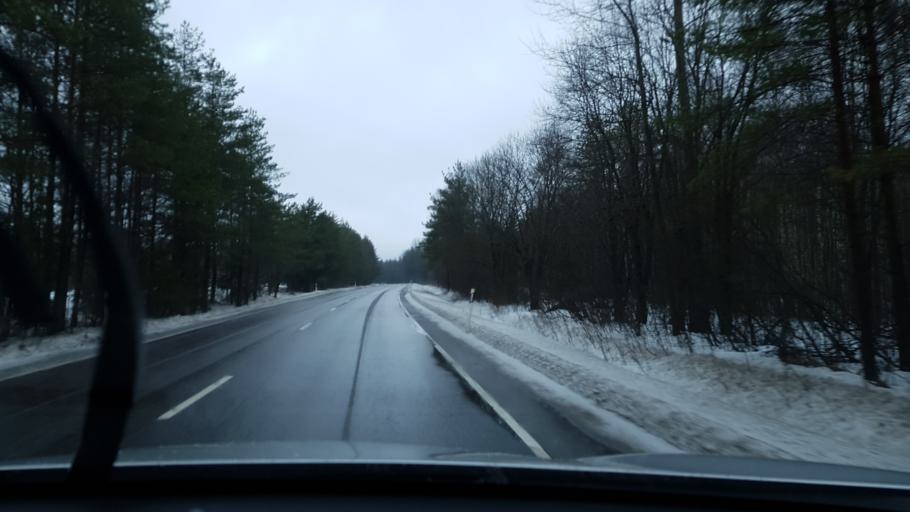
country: EE
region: Raplamaa
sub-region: Kehtna vald
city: Kehtna
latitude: 58.8722
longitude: 24.9869
